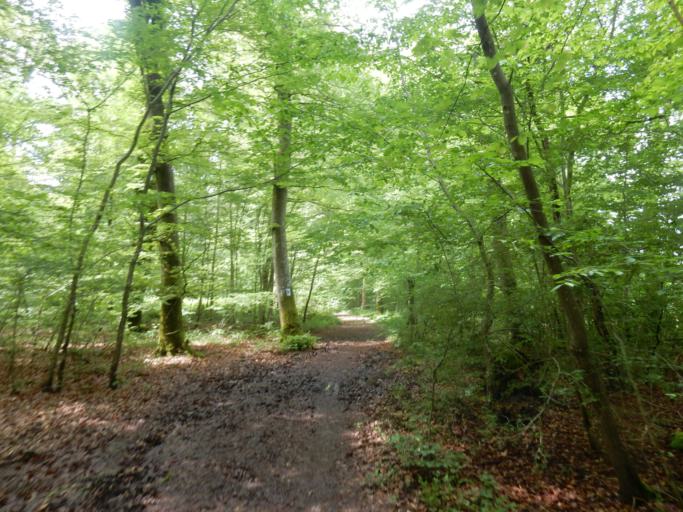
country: LU
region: Diekirch
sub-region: Canton de Redange
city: Vichten
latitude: 49.7999
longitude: 6.0256
